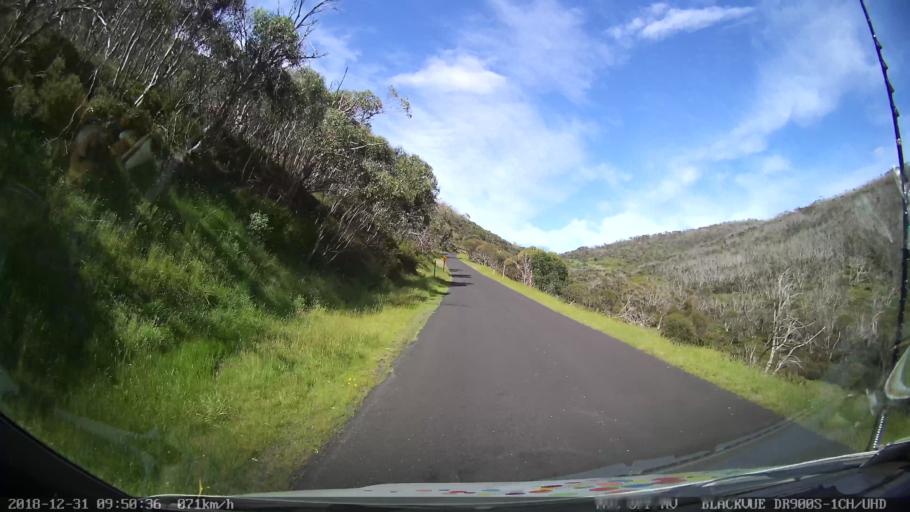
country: AU
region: New South Wales
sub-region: Snowy River
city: Jindabyne
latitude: -36.5209
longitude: 148.2712
